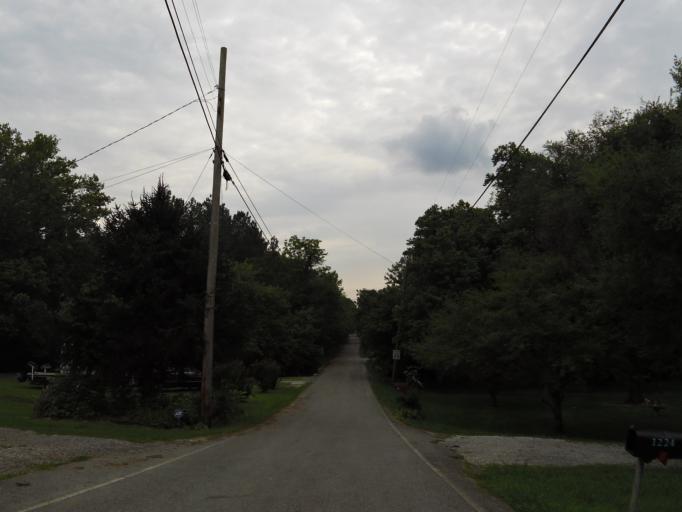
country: US
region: Tennessee
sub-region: Sevier County
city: Seymour
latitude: 35.9244
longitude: -83.7963
